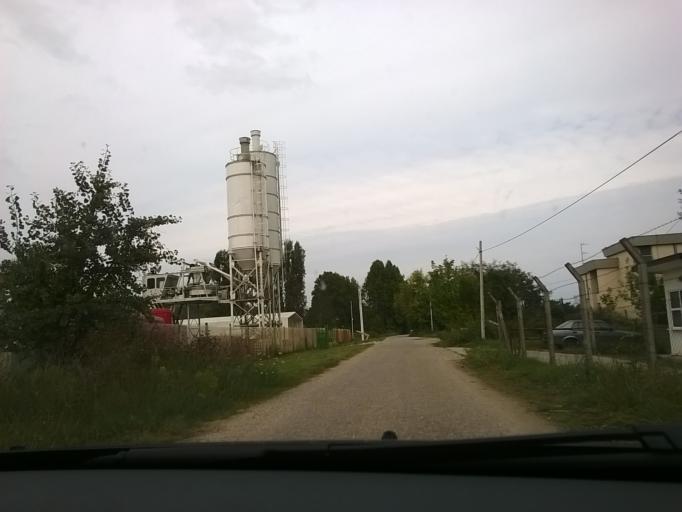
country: RS
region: Autonomna Pokrajina Vojvodina
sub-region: Juznobanatski Okrug
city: Pancevo
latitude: 44.8548
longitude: 20.6404
